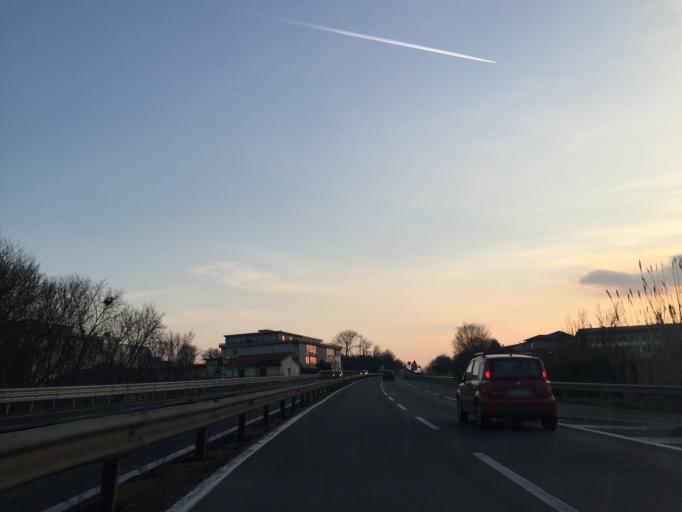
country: IT
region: Campania
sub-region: Provincia di Avellino
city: Atripalda
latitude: 40.9271
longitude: 14.8293
